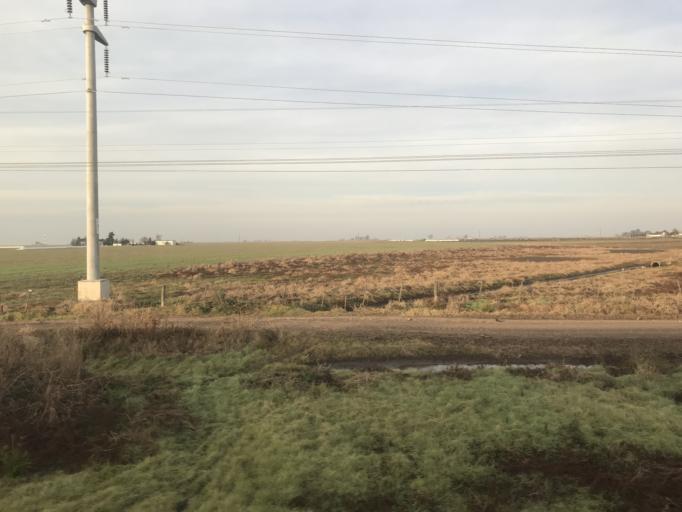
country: AR
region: Cordoba
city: Marcos Juarez
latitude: -32.6836
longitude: -62.1933
